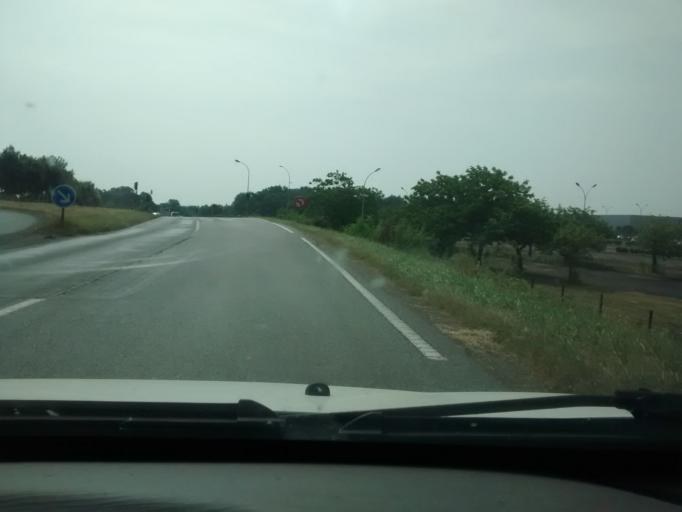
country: FR
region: Brittany
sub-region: Departement d'Ille-et-Vilaine
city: Saint-Jacques-de-la-Lande
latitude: 48.0634
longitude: -1.7016
